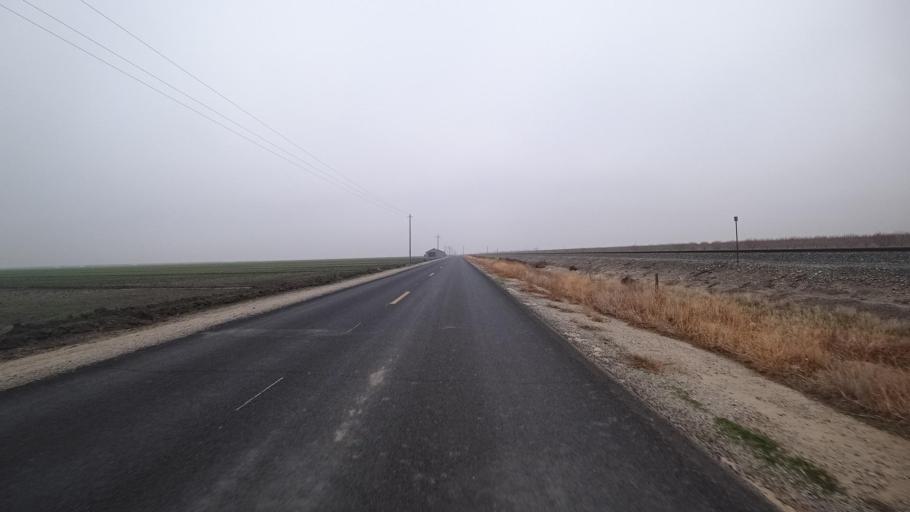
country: US
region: California
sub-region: Kern County
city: Greenfield
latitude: 35.1801
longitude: -119.1779
